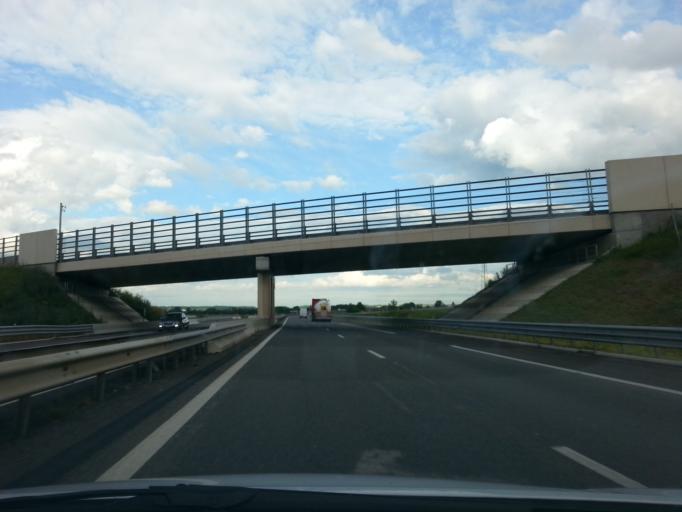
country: FR
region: Rhone-Alpes
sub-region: Departement de l'Ain
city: Trevoux
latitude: 45.9279
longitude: 4.7477
